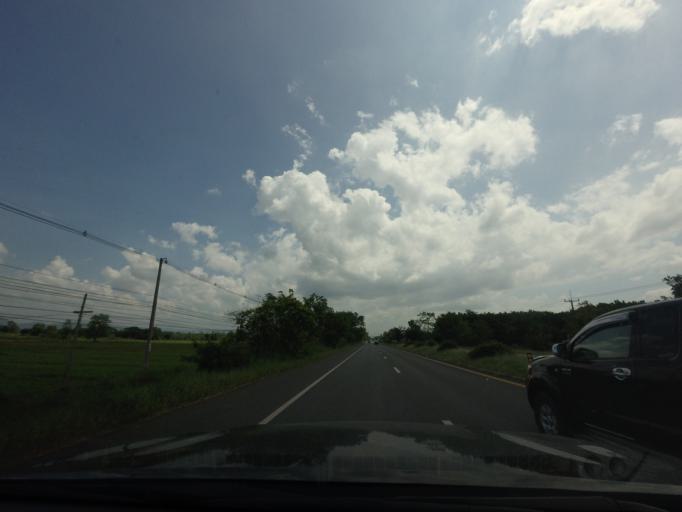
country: TH
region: Phetchabun
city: Phetchabun
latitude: 16.2388
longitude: 101.0784
